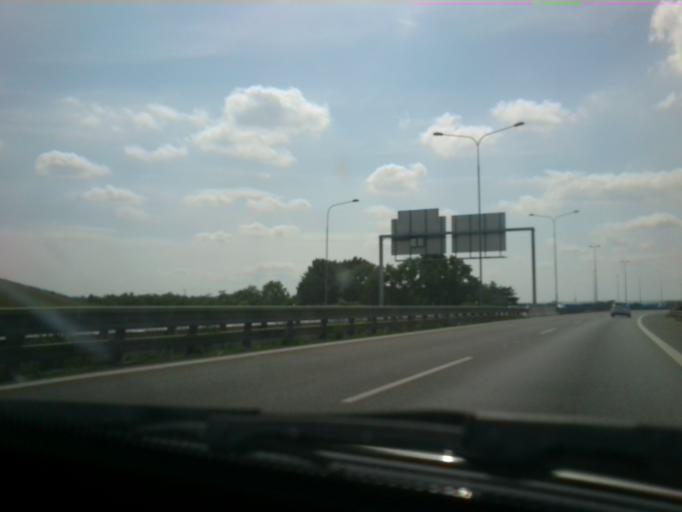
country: CZ
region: Praha
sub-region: Praha 19
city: Satalice
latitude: 50.1175
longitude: 14.5815
